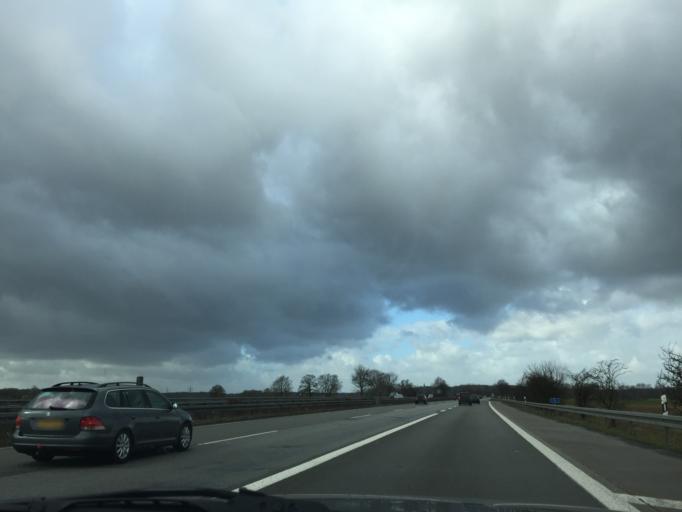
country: NL
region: Gelderland
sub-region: Gemeente Montferland
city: s-Heerenberg
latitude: 51.8635
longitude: 6.2394
